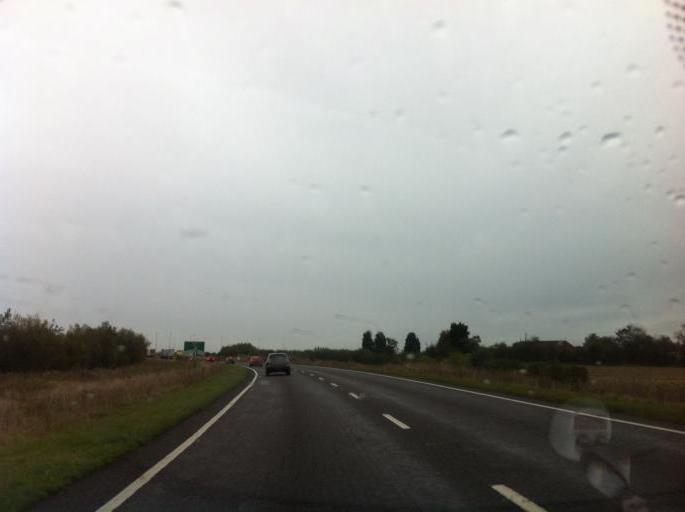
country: GB
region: England
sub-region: Peterborough
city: Newborough
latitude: 52.6349
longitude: -0.1979
